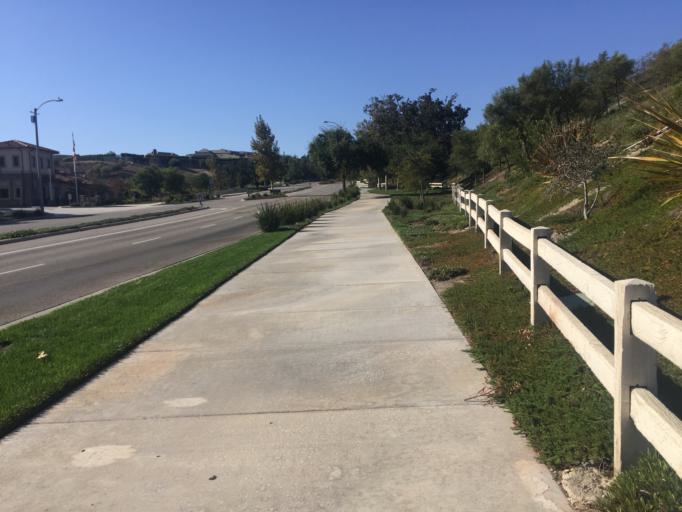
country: US
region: California
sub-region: Ventura County
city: Simi Valley
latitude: 34.2882
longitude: -118.7617
